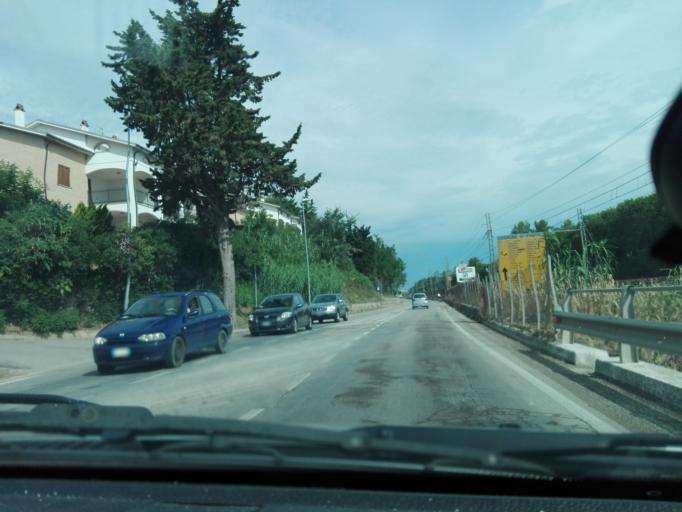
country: IT
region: Abruzzo
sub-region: Provincia di Teramo
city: Pineto
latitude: 42.5897
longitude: 14.0840
